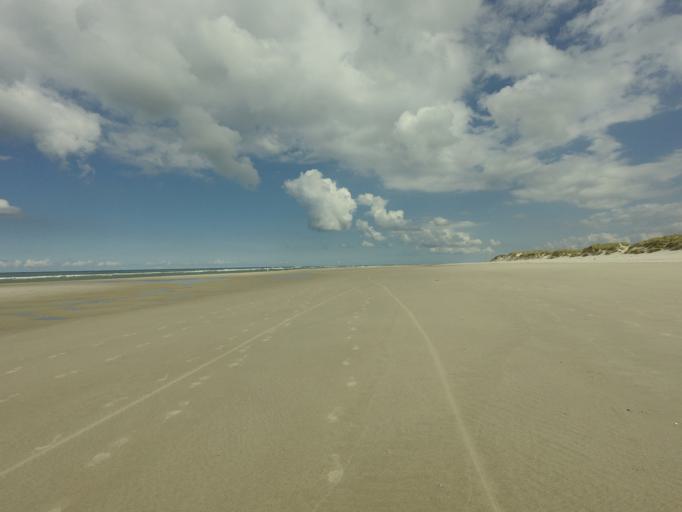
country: NL
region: Friesland
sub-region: Gemeente Terschelling
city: West-Terschelling
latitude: 53.3986
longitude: 5.2211
